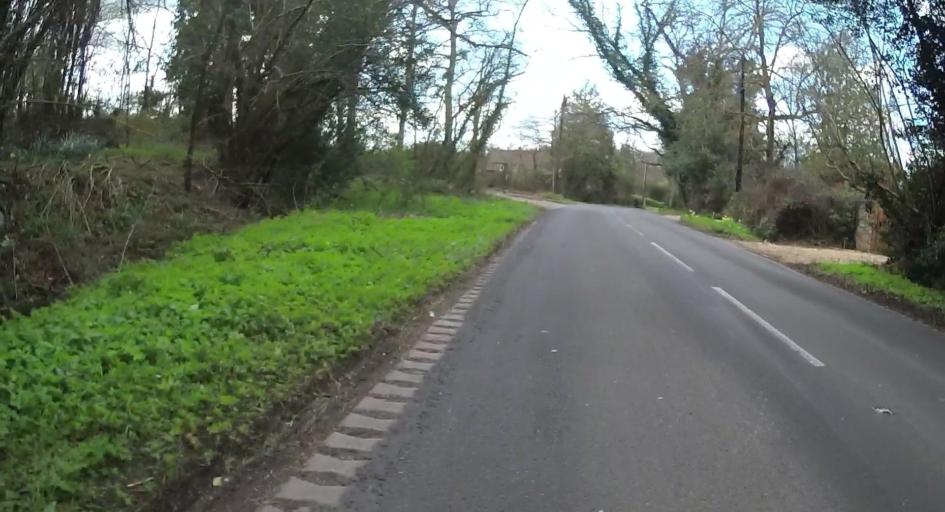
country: GB
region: England
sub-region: Surrey
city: Knaphill
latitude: 51.3350
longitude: -0.6241
